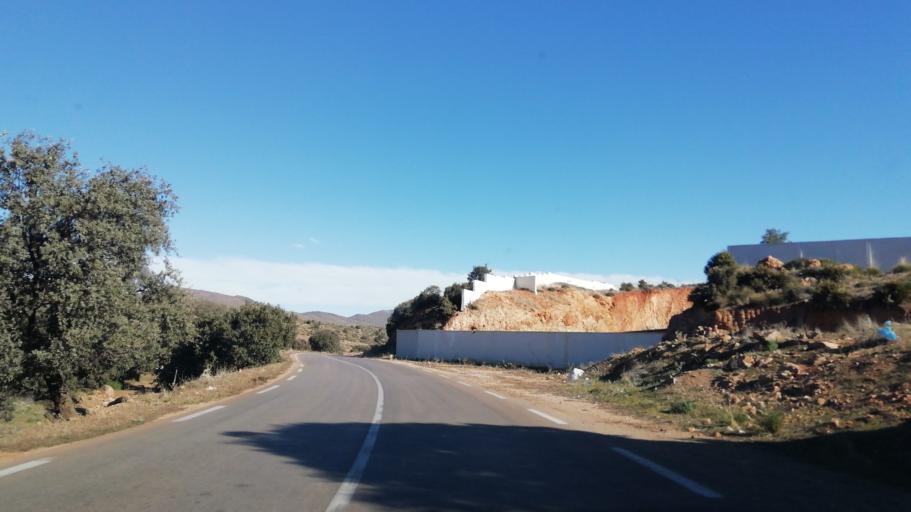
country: DZ
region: Tlemcen
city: Ouled Mimoun
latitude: 34.7600
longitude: -1.1450
